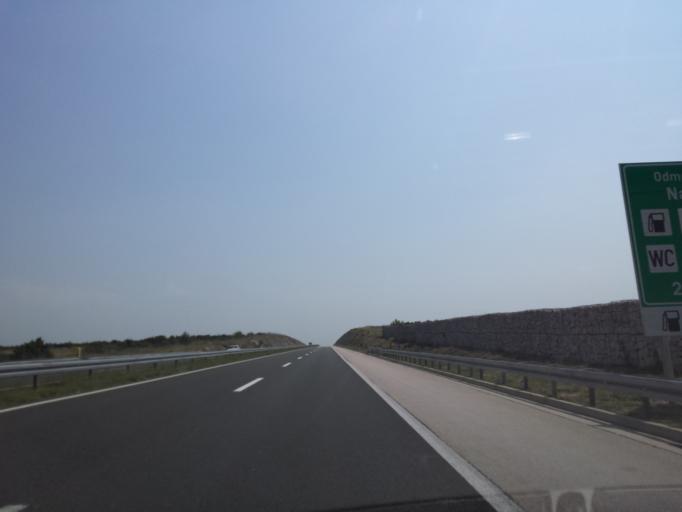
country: HR
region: Zadarska
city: Polaca
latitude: 44.0790
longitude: 15.5099
